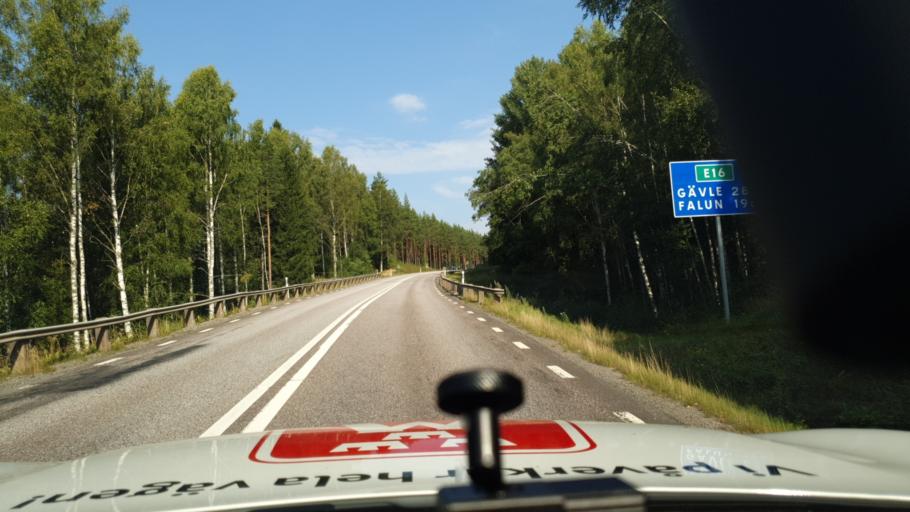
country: SE
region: Vaermland
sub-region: Hagfors Kommun
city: Ekshaerad
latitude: 60.4254
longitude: 13.2574
